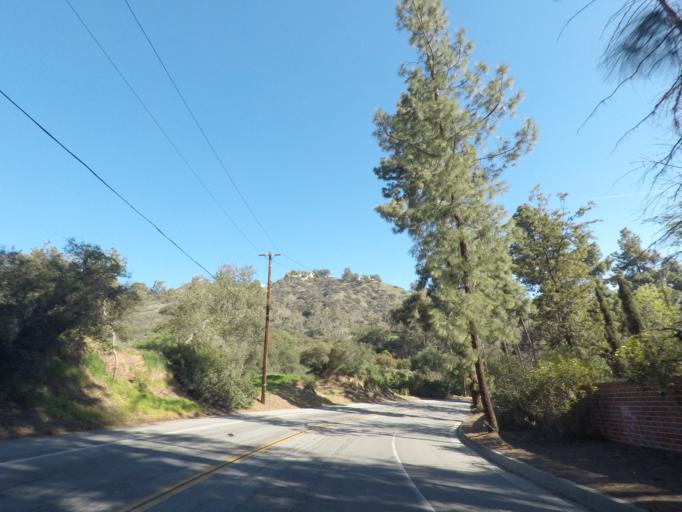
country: US
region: California
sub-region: Los Angeles County
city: La Canada Flintridge
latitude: 34.1719
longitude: -118.1878
